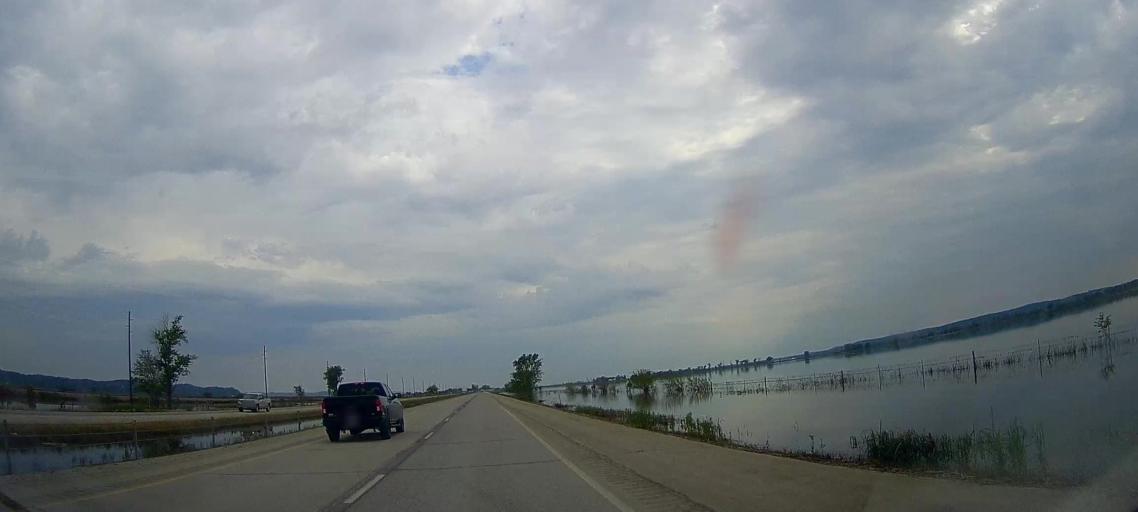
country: US
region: Iowa
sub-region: Harrison County
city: Missouri Valley
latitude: 41.4447
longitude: -95.8998
